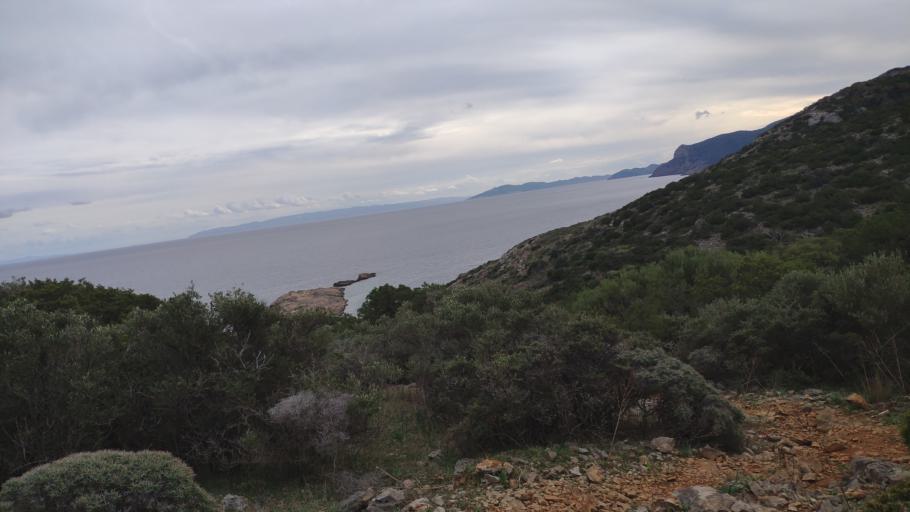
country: GR
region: Attica
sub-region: Nomarchia Anatolikis Attikis
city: Limin Mesoyaias
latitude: 37.9052
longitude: 24.0427
